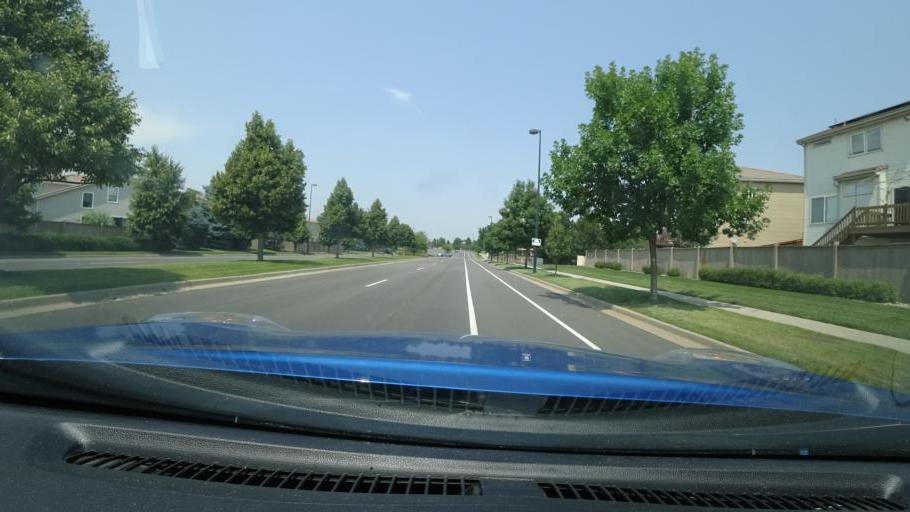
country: US
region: Colorado
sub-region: Adams County
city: Aurora
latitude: 39.7738
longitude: -104.7533
